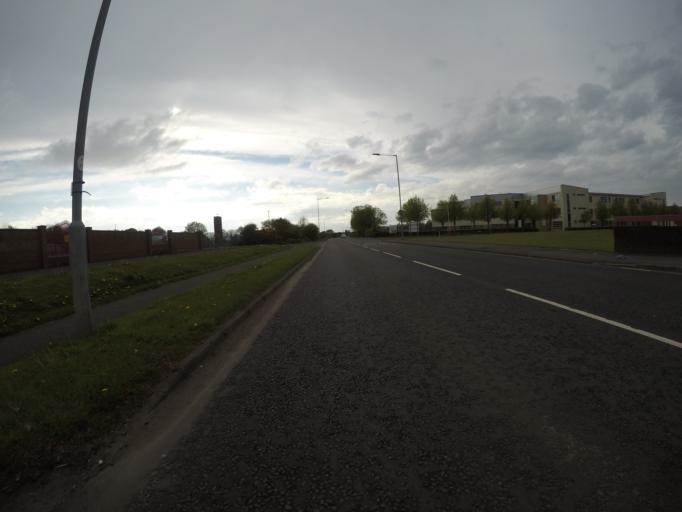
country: GB
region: Scotland
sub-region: North Ayrshire
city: Dreghorn
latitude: 55.6070
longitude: -4.6323
